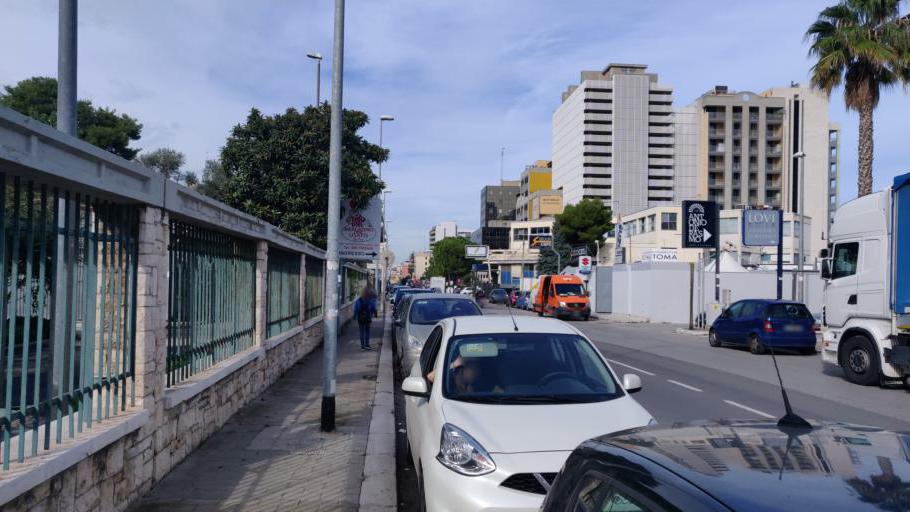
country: IT
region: Apulia
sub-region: Provincia di Bari
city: Bari
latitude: 41.1113
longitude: 16.8829
